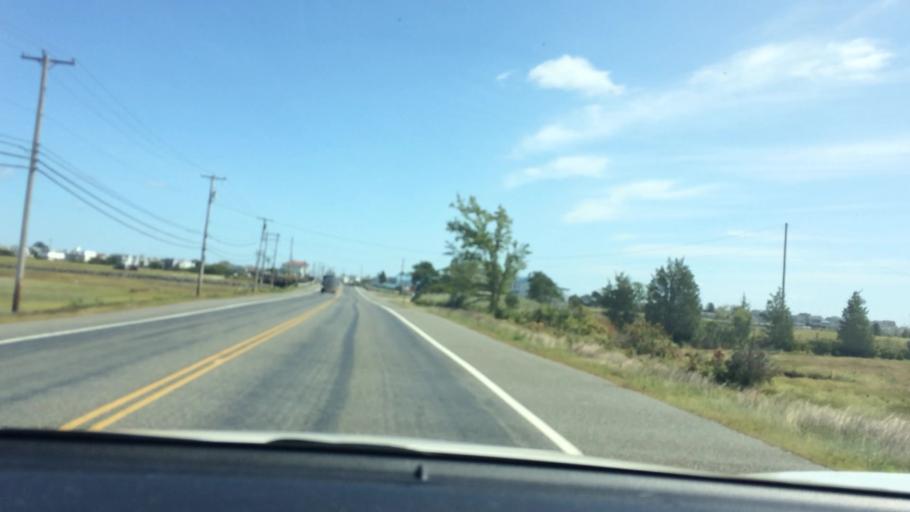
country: US
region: New Hampshire
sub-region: Rockingham County
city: Hampton Beach
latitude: 42.8706
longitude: -70.8273
